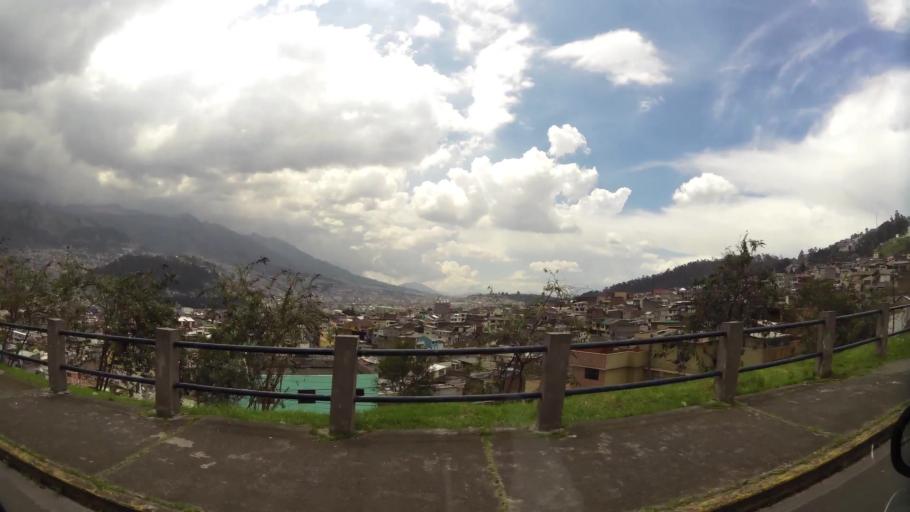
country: EC
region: Pichincha
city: Quito
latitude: -0.2493
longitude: -78.5109
